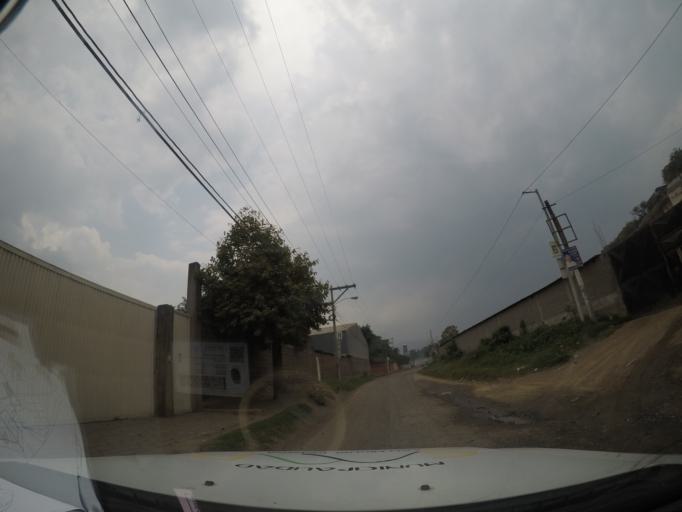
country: GT
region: Guatemala
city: Petapa
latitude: 14.5095
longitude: -90.5557
